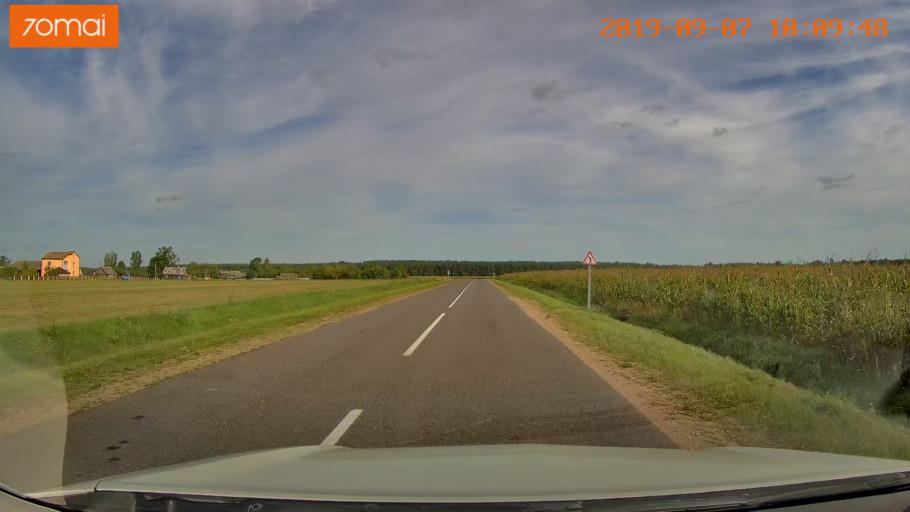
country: BY
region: Grodnenskaya
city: Voranava
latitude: 54.1008
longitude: 25.3730
